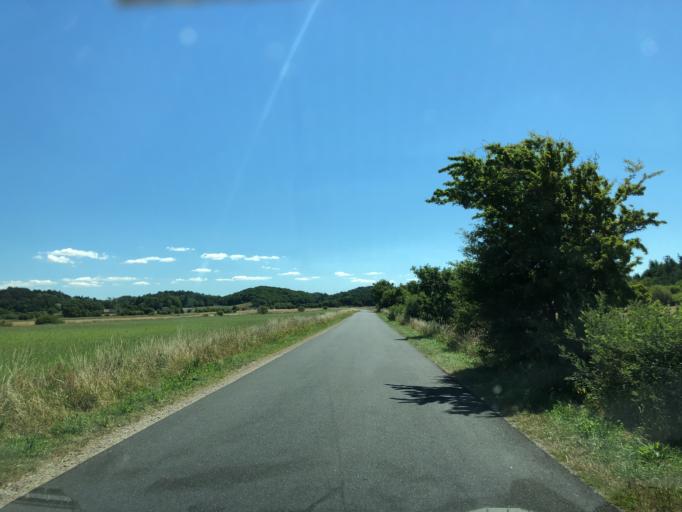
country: DK
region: Central Jutland
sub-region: Viborg Kommune
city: Viborg
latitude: 56.5459
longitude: 9.4386
